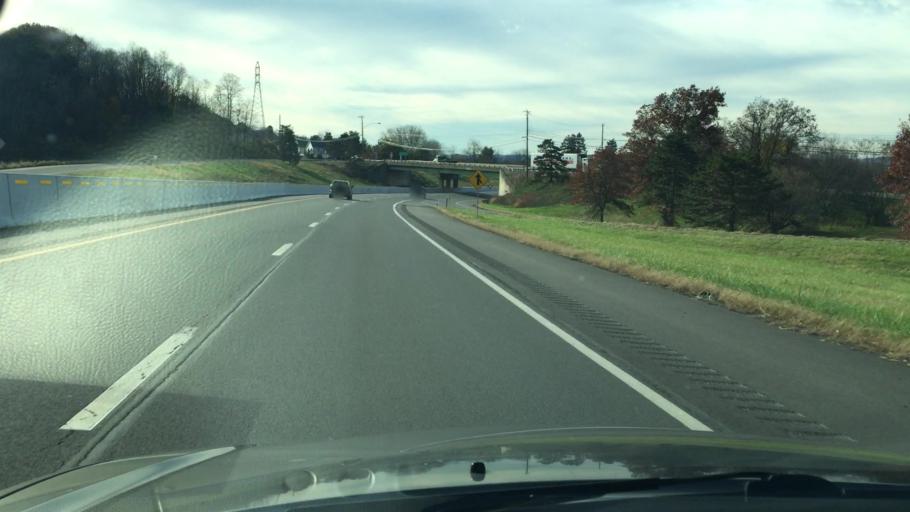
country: US
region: Pennsylvania
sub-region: Luzerne County
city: Ashley
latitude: 41.1999
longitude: -75.9178
